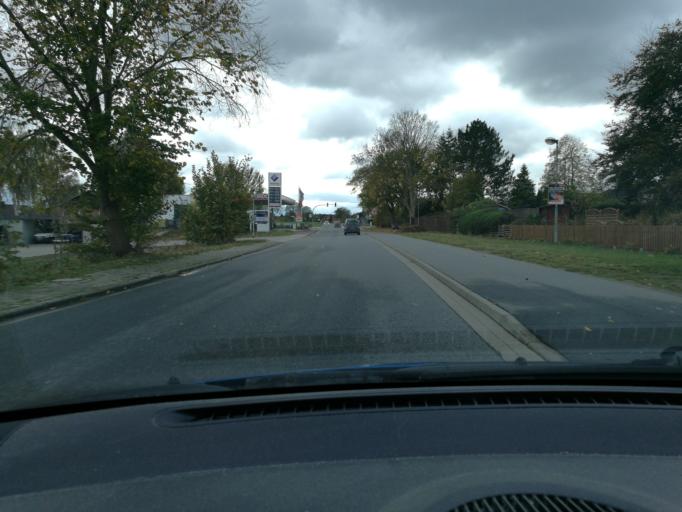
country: DE
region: Schleswig-Holstein
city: Gross Sarau
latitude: 53.7729
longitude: 10.7382
